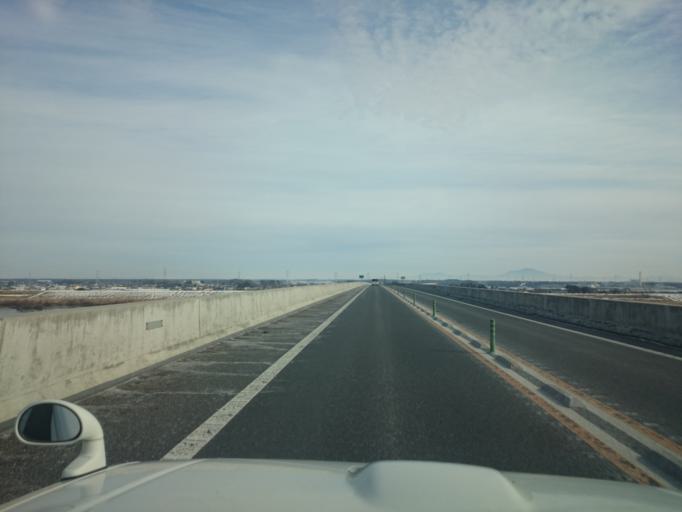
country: JP
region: Ibaraki
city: Sakai
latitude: 36.1151
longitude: 139.7649
